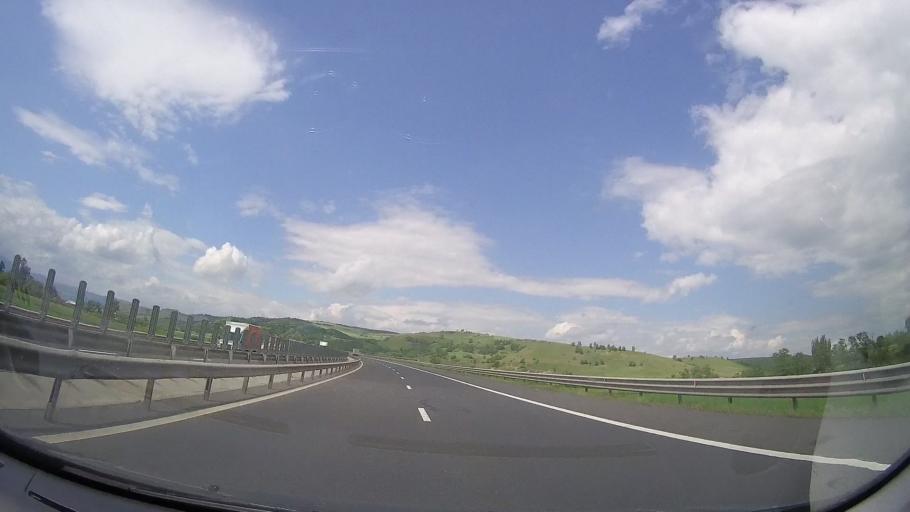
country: RO
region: Alba
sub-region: Municipiul Sebes
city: Sebes
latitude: 45.9621
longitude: 23.5960
